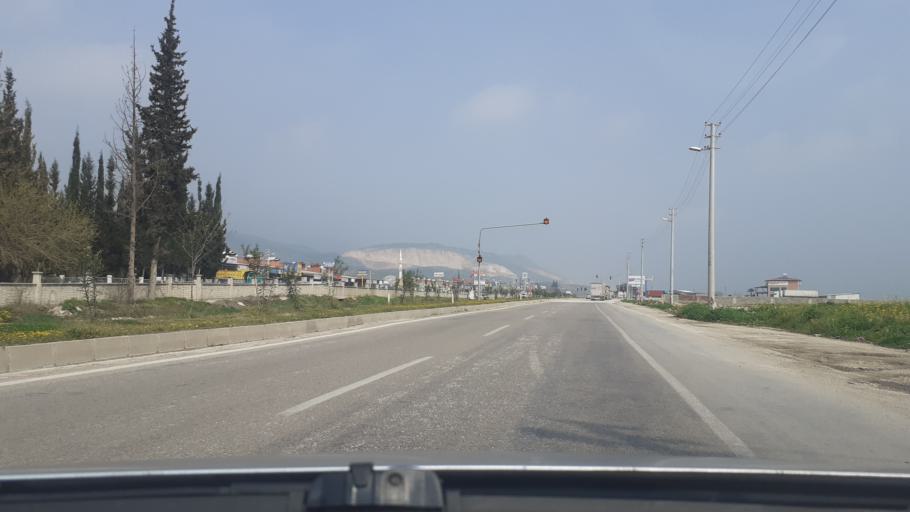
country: TR
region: Hatay
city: Kirikhan
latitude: 36.5211
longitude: 36.3768
